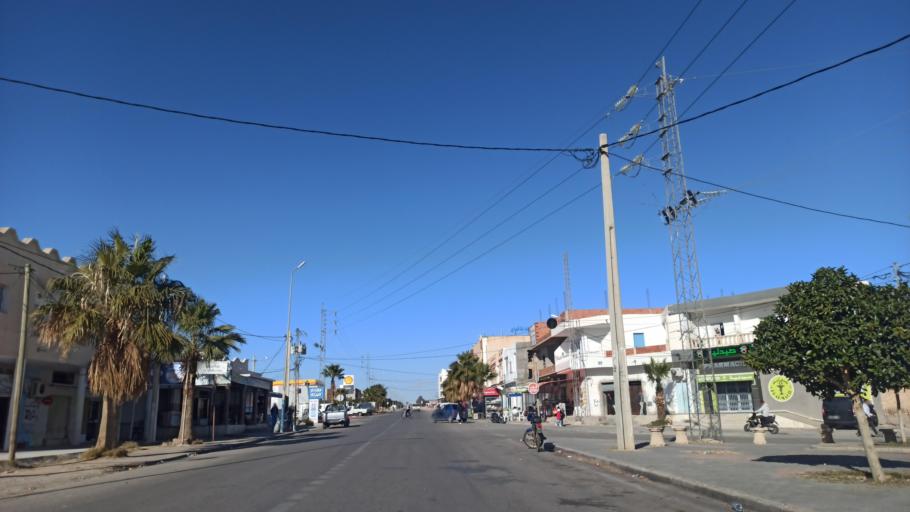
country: TN
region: Sidi Bu Zayd
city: Jilma
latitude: 35.2783
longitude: 9.4189
